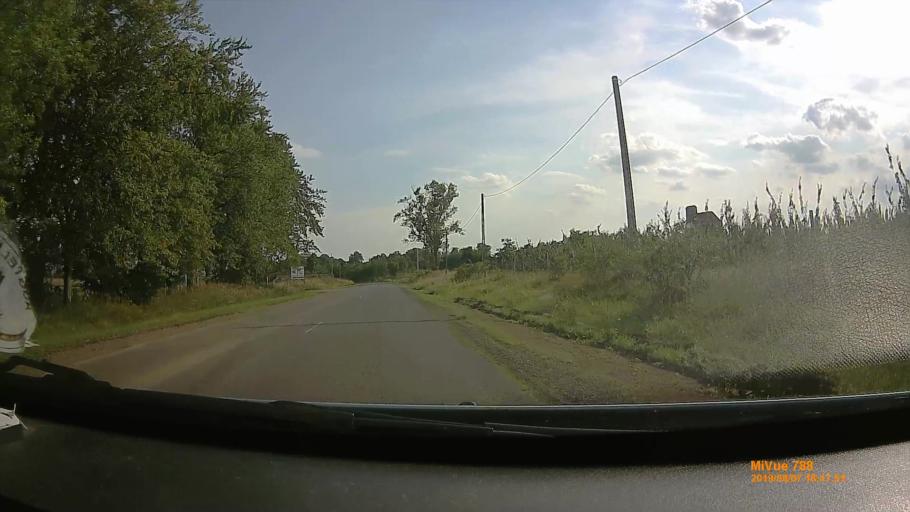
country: HU
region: Borsod-Abauj-Zemplen
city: Abaujszanto
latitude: 48.3375
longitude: 21.2057
